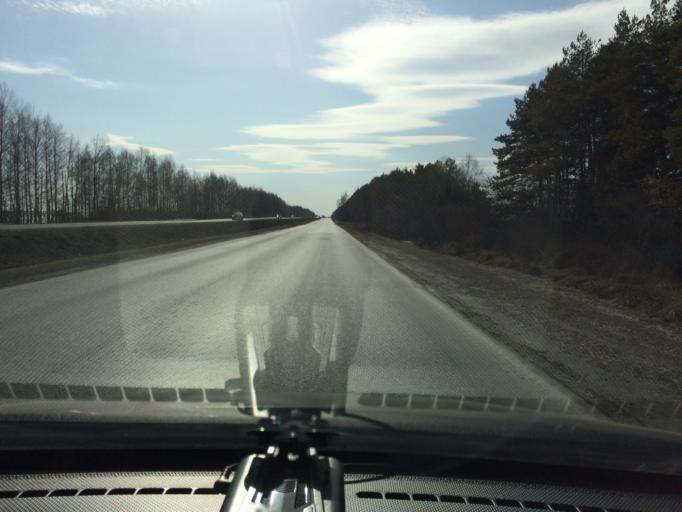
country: RU
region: Mariy-El
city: Yoshkar-Ola
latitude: 56.7317
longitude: 48.1500
